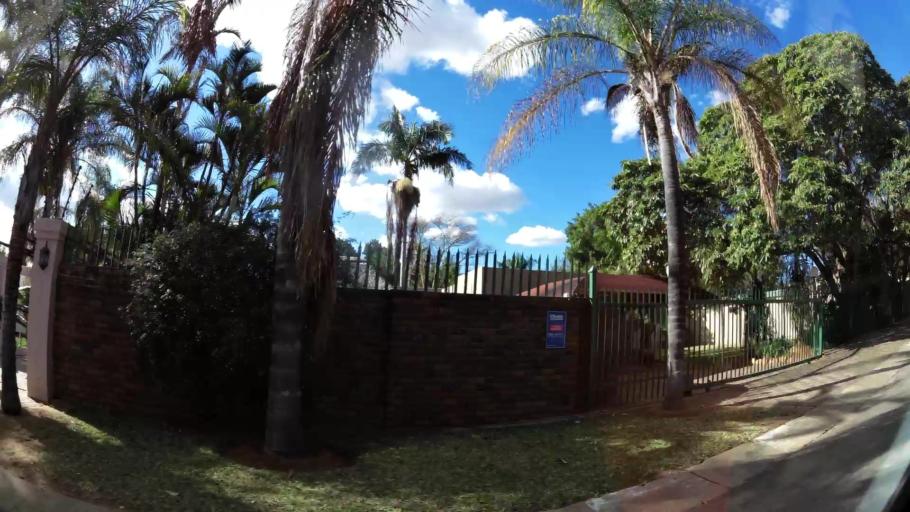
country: ZA
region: Limpopo
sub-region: Capricorn District Municipality
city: Polokwane
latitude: -23.8925
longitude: 29.4690
